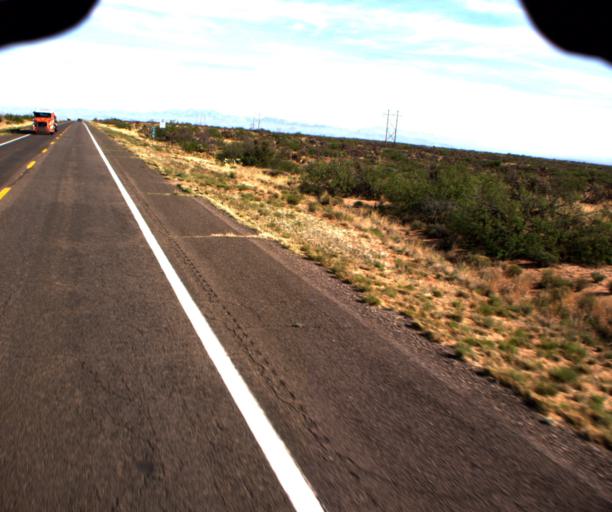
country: US
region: Arizona
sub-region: Graham County
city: Swift Trail Junction
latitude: 32.6205
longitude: -109.6889
